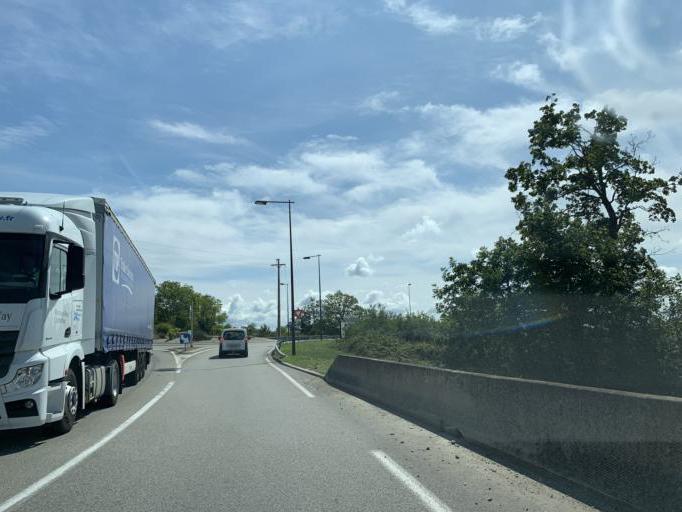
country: FR
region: Rhone-Alpes
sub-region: Departement de l'Ain
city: Nievroz
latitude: 45.8360
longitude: 5.0655
